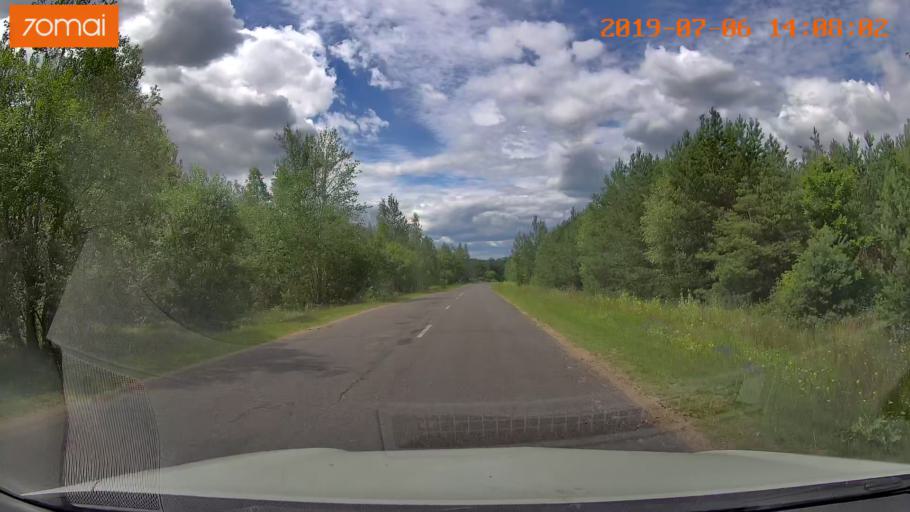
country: BY
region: Minsk
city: Ivyanyets
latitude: 53.8720
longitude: 26.7623
